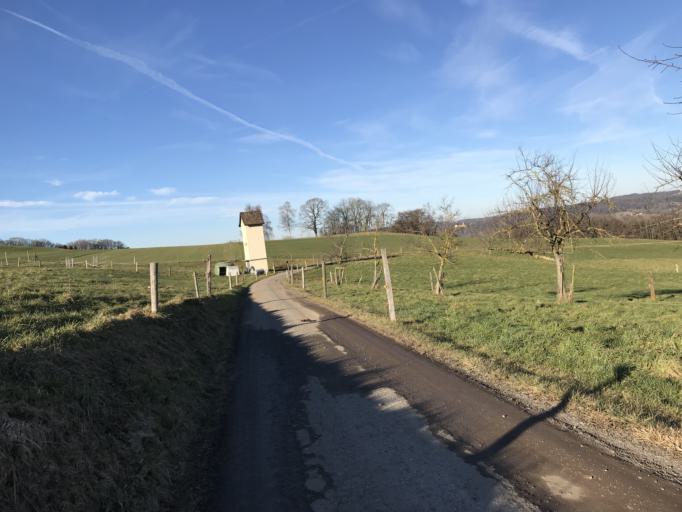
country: CH
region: Thurgau
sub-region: Frauenfeld District
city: Eschenz
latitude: 47.6341
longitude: 8.8554
